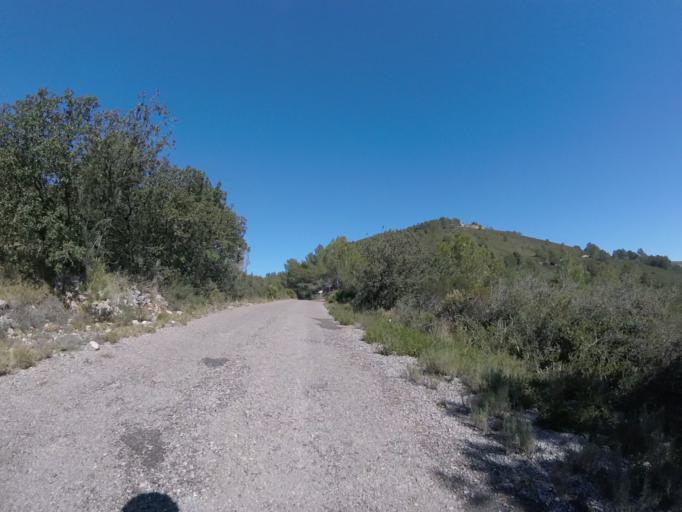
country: ES
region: Valencia
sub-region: Provincia de Castello
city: Cervera del Maestre
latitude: 40.4091
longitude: 0.1988
